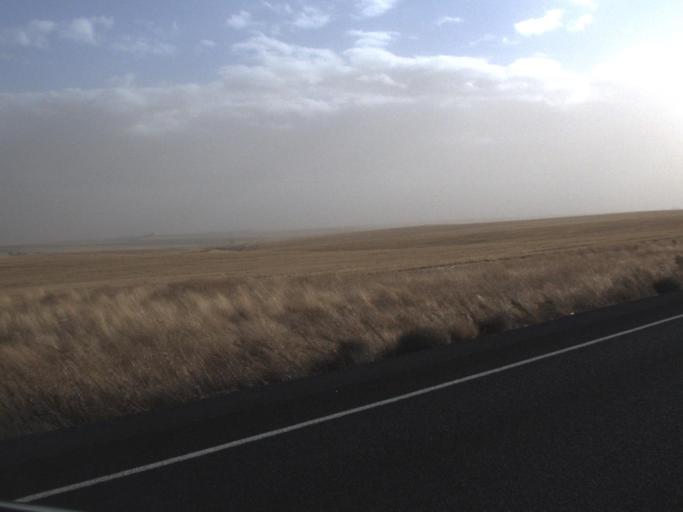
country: US
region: Washington
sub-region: Lincoln County
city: Davenport
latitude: 47.4497
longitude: -118.3164
